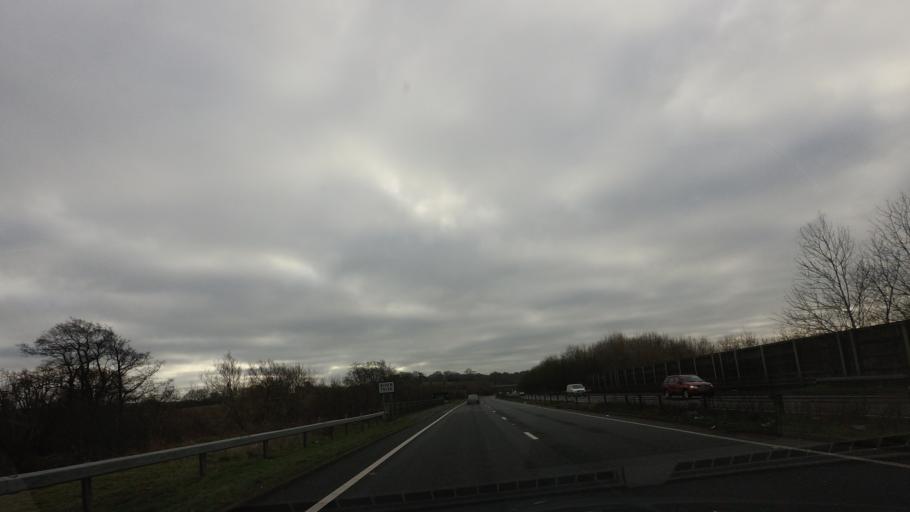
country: GB
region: England
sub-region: East Sussex
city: Wadhurst
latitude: 51.1031
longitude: 0.4050
